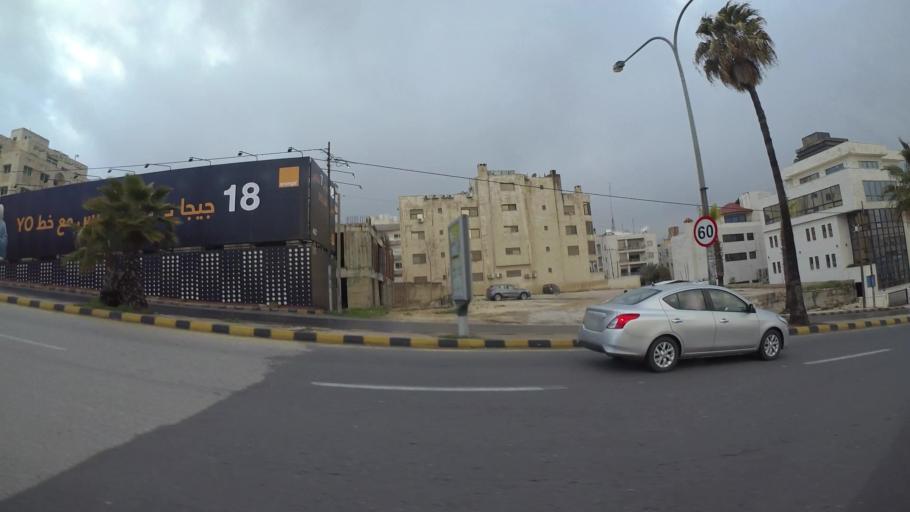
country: JO
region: Amman
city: Amman
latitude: 31.9636
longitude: 35.8836
